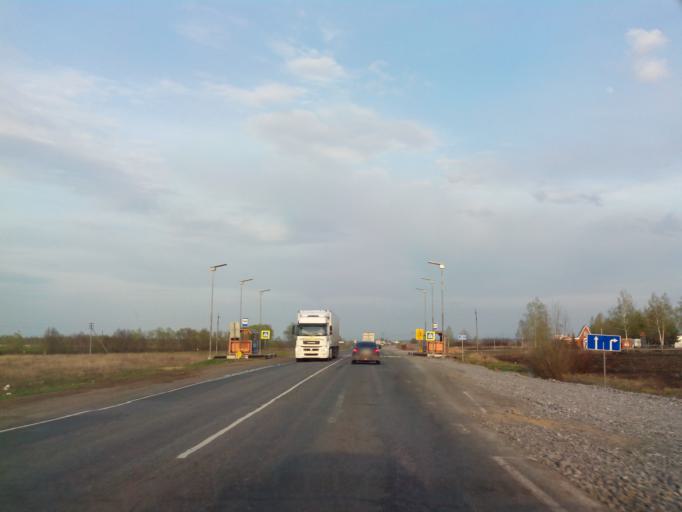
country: RU
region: Rjazan
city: Korablino
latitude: 53.7513
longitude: 39.8444
